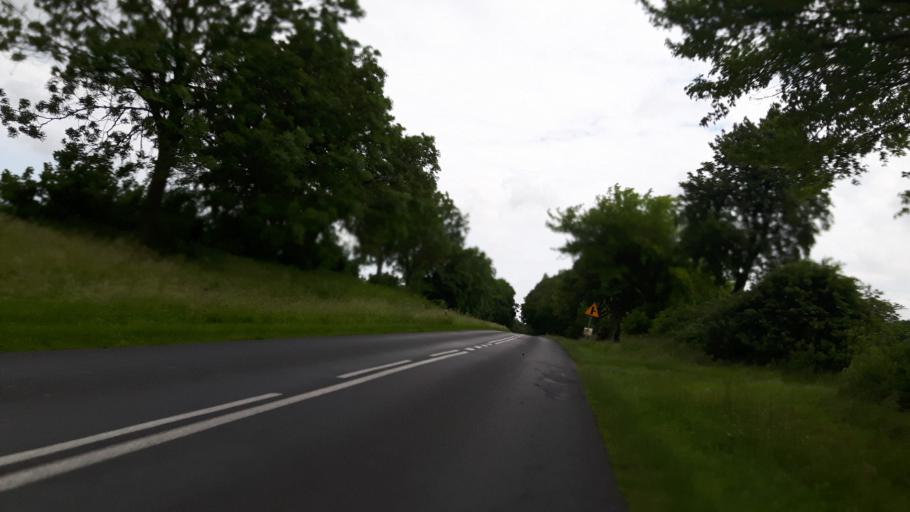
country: PL
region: West Pomeranian Voivodeship
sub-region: Powiat gryficki
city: Gryfice
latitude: 53.9532
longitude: 15.2265
